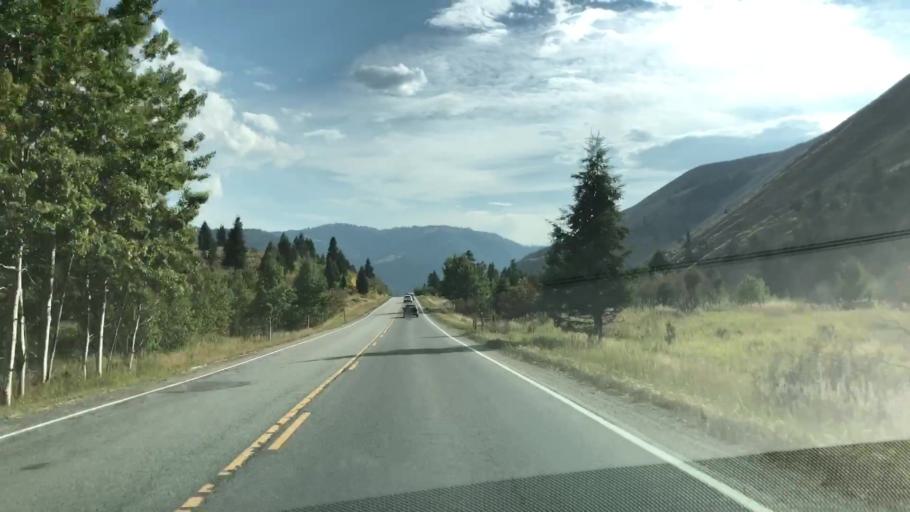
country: US
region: Wyoming
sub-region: Teton County
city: Hoback
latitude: 43.3359
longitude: -110.7255
